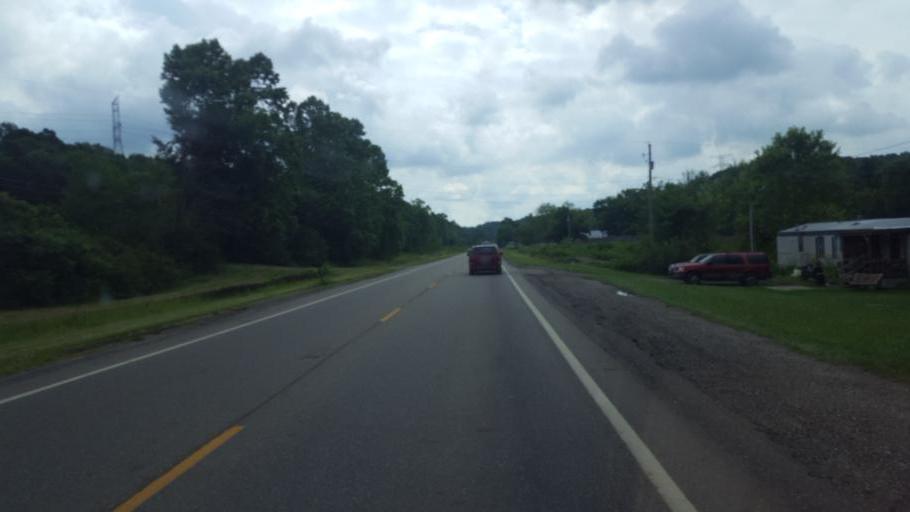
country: US
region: Ohio
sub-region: Columbiana County
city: Lisbon
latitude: 40.7692
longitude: -80.7423
